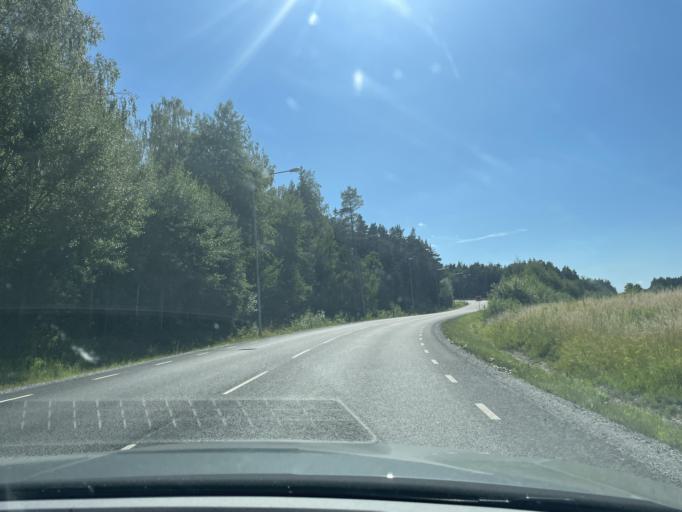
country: SE
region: Stockholm
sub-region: Sigtuna Kommun
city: Marsta
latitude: 59.6228
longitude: 17.8223
